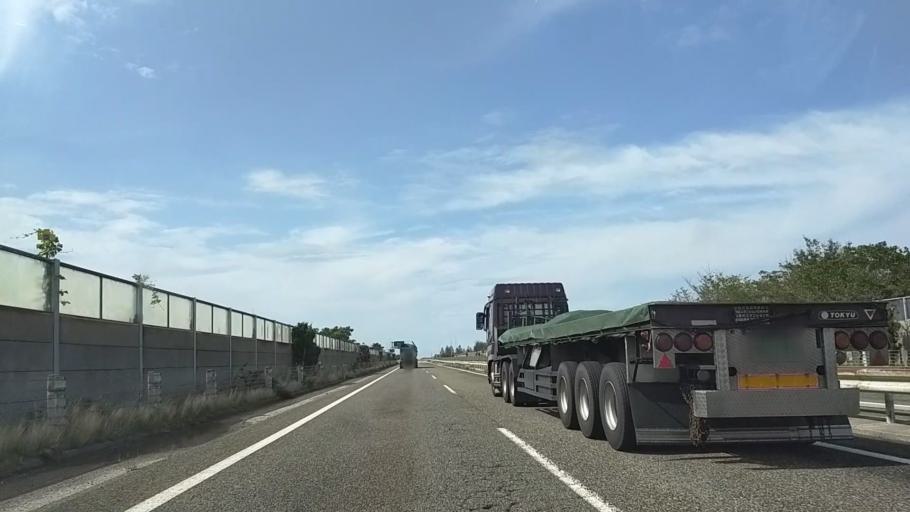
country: JP
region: Toyama
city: Nyuzen
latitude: 36.9432
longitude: 137.5565
